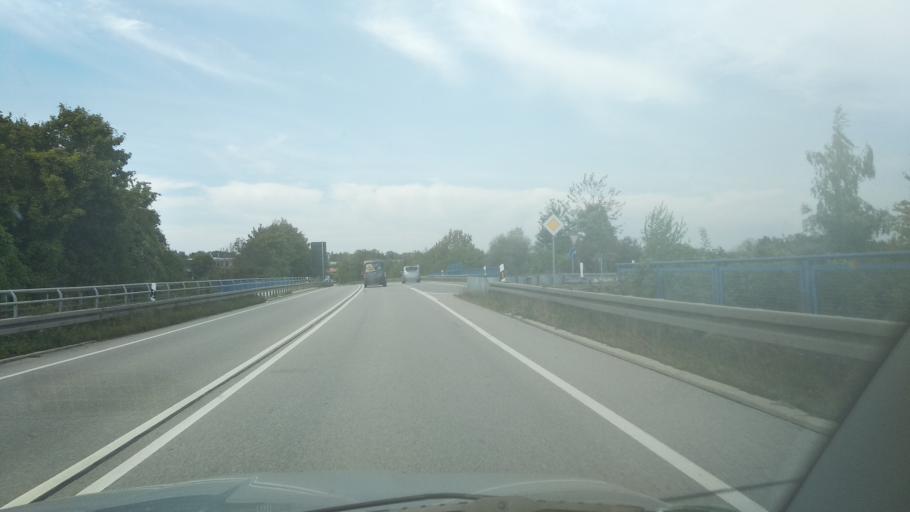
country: DE
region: Bavaria
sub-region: Upper Bavaria
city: Ismaning
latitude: 48.2347
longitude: 11.6856
